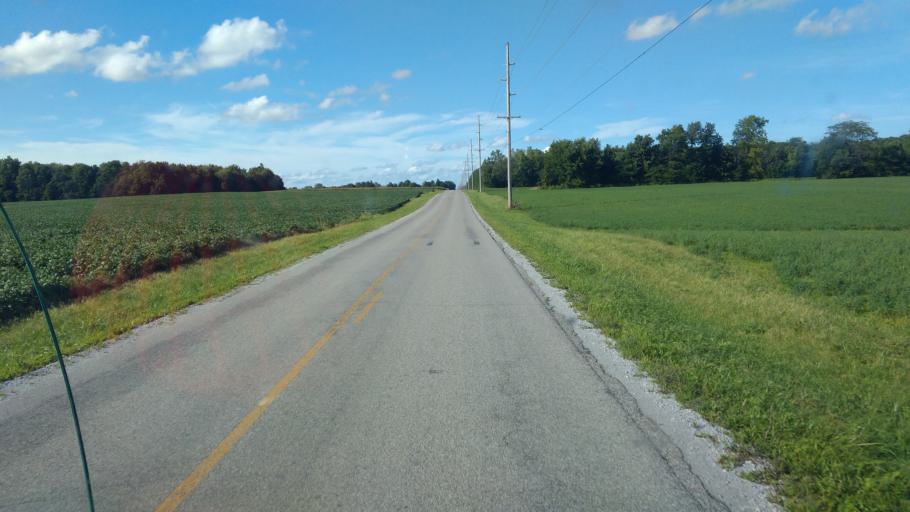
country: US
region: Ohio
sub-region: Hardin County
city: Kenton
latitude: 40.7063
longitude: -83.6535
